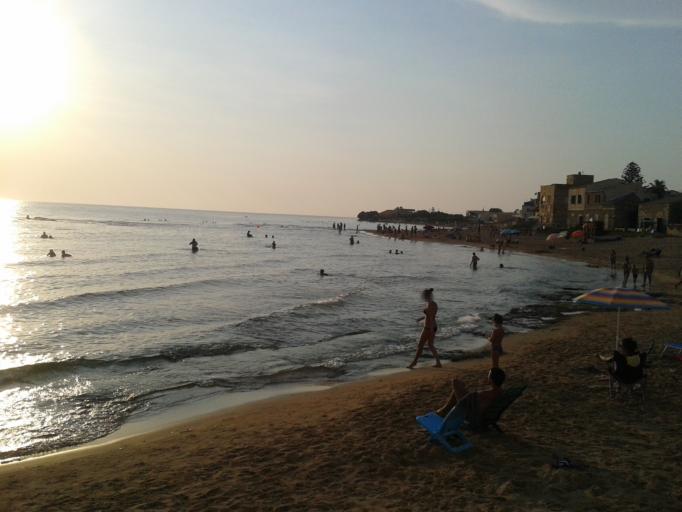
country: IT
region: Sicily
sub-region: Ragusa
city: Santa Croce Camerina
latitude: 36.7886
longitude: 14.4930
